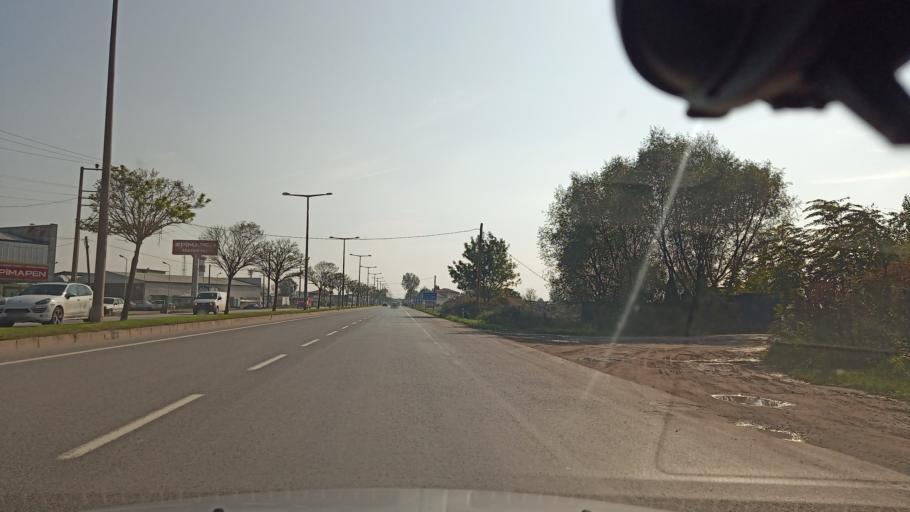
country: TR
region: Sakarya
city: Adapazari
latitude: 40.8205
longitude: 30.3976
